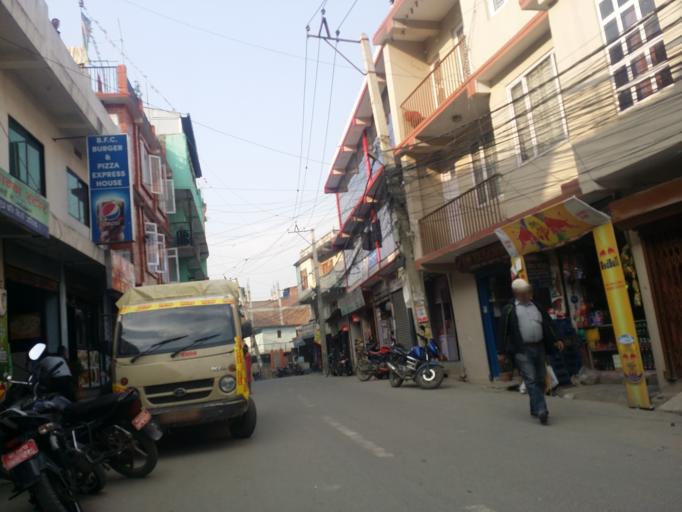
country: NP
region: Central Region
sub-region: Bagmati Zone
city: Kathmandu
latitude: 27.6994
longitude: 85.3457
